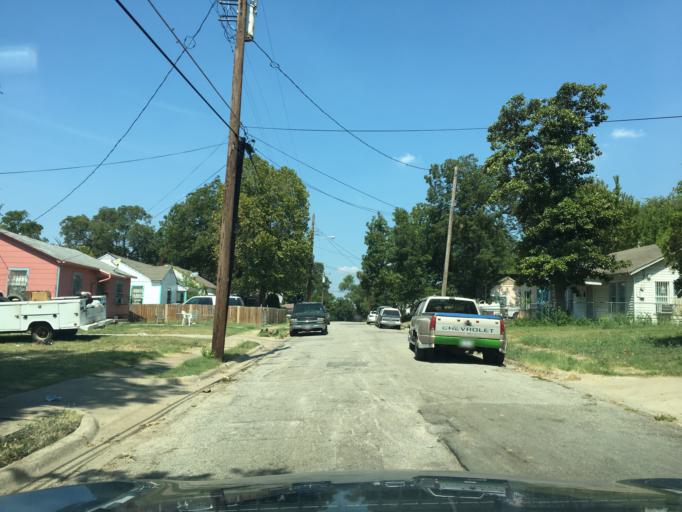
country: US
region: Texas
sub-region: Dallas County
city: Dallas
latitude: 32.7440
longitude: -96.7918
